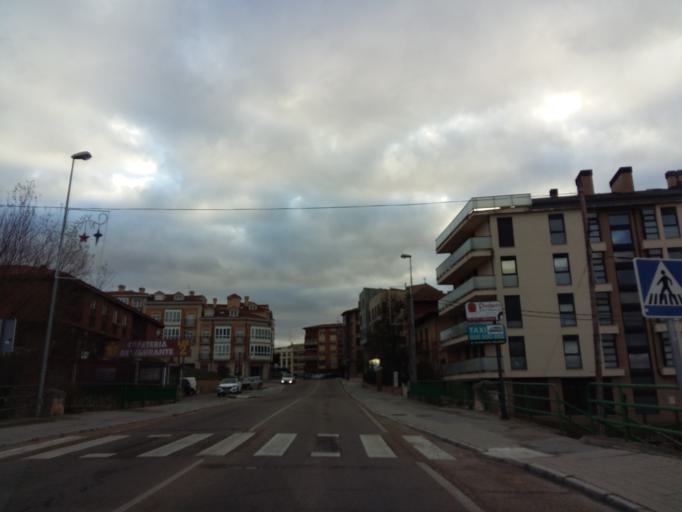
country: ES
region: Castille and Leon
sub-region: Provincia de Burgos
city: Lerma
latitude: 42.0281
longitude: -3.7600
